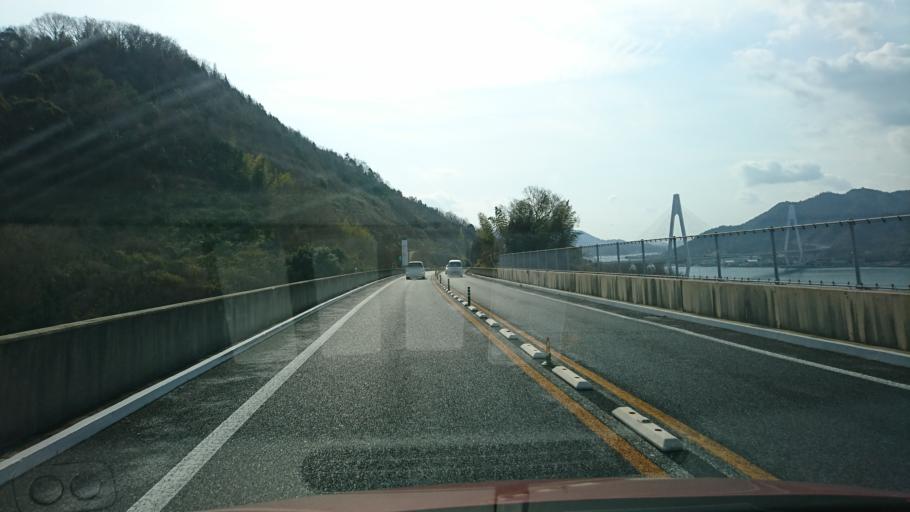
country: JP
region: Hiroshima
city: Innoshima
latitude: 34.3130
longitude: 133.1557
